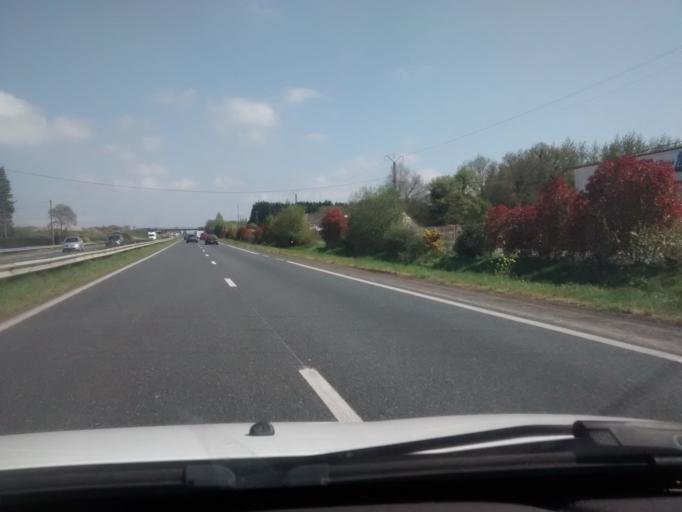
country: FR
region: Brittany
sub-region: Departement des Cotes-d'Armor
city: Saint-Agathon
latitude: 48.5454
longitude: -3.0911
